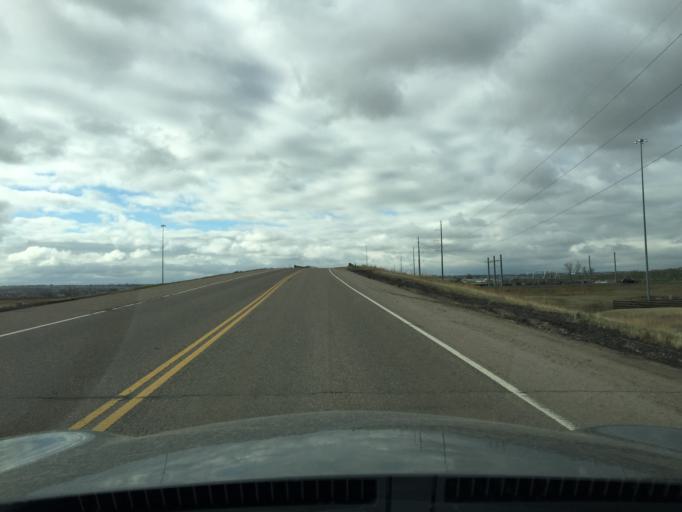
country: US
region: Colorado
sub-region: Adams County
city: Northglenn
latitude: 39.9817
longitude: -104.9782
